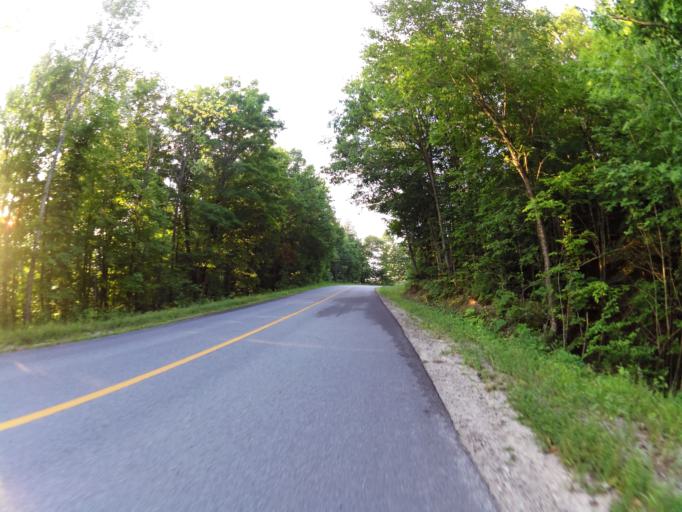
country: CA
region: Quebec
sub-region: Outaouais
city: Wakefield
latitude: 45.7255
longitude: -75.9695
